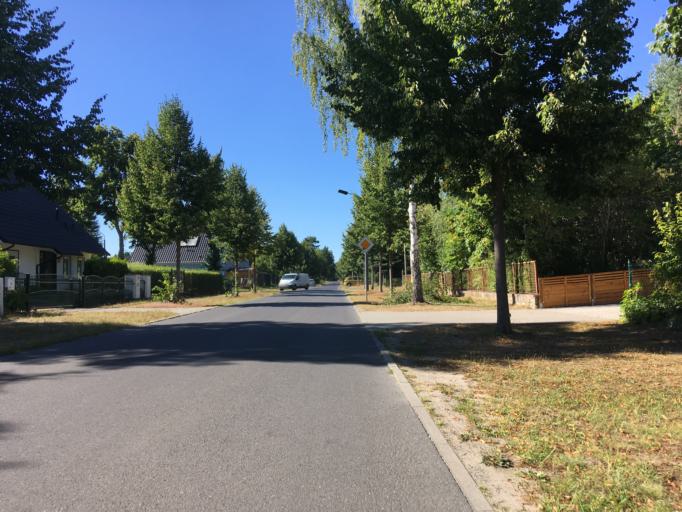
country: DE
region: Brandenburg
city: Schulzendorf
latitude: 52.3486
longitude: 13.5990
